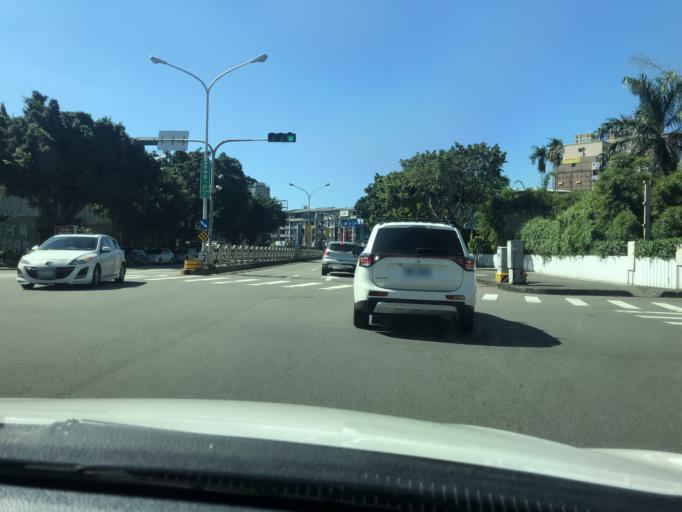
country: TW
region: Taiwan
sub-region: Taichung City
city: Taichung
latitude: 24.1561
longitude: 120.6856
